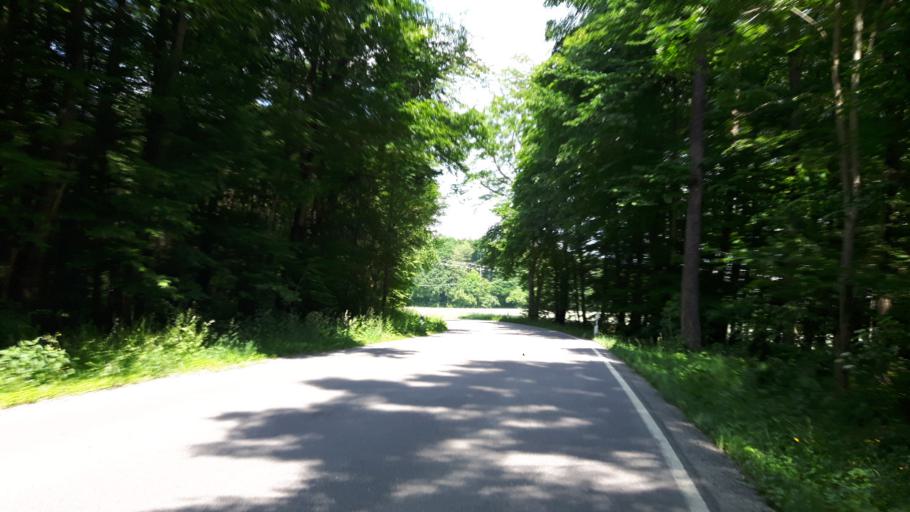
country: DE
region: Baden-Wuerttemberg
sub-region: Regierungsbezirk Stuttgart
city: Jagsthausen
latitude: 49.3121
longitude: 9.5145
